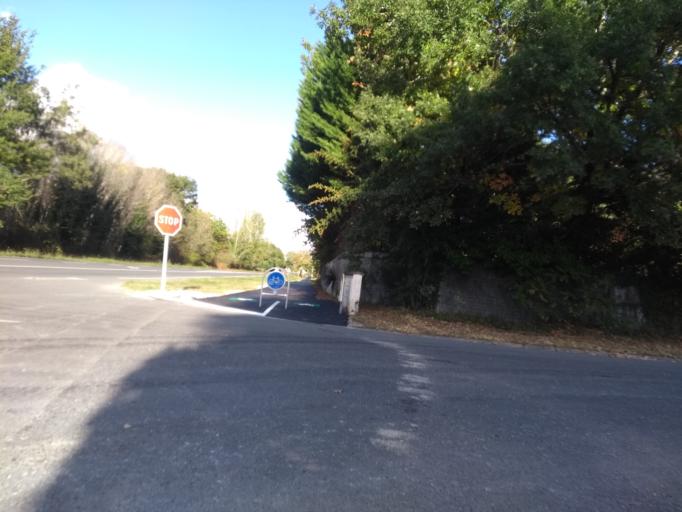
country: FR
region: Aquitaine
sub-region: Departement de la Gironde
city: Cestas
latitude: 44.7283
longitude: -0.6731
